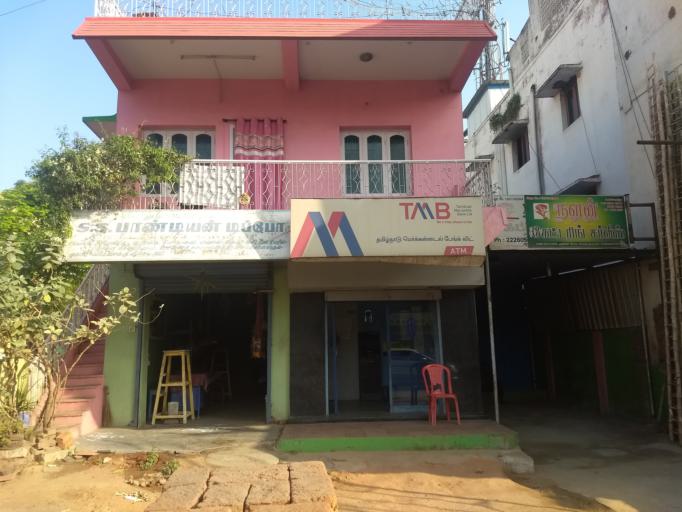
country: IN
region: Tamil Nadu
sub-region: Kancheepuram
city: Vandalur
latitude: 12.9257
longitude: 80.1022
